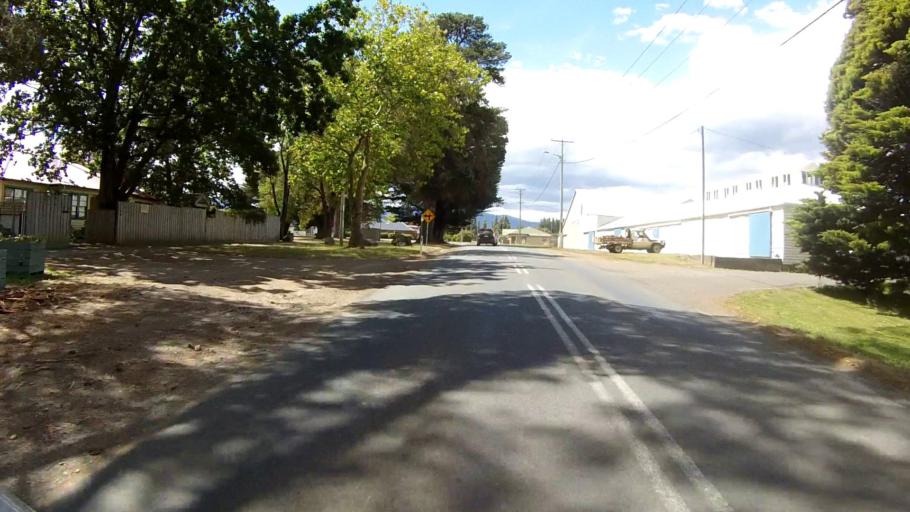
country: AU
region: Tasmania
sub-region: Huon Valley
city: Huonville
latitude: -43.0154
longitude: 147.0405
